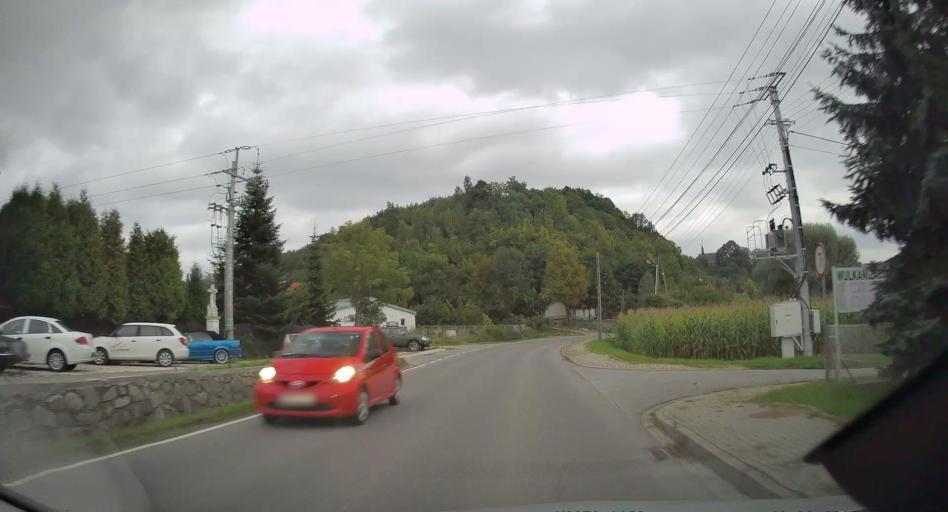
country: PL
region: Lesser Poland Voivodeship
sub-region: Powiat krakowski
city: Slomniki
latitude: 50.1506
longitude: 20.1069
